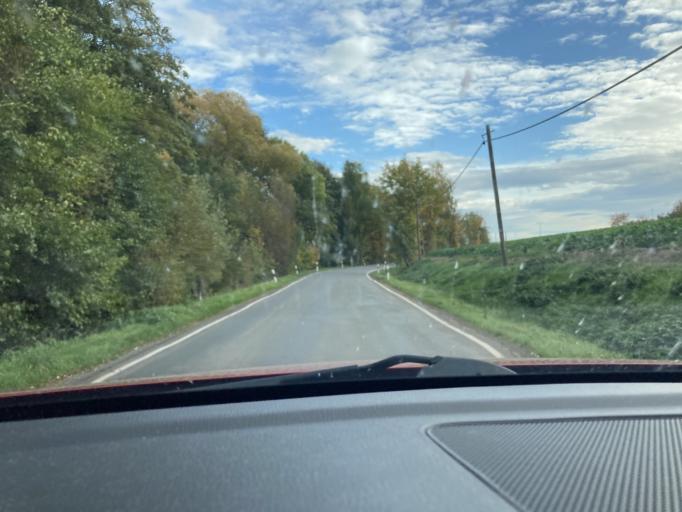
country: DE
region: Thuringia
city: Friedrichsthal
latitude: 51.5206
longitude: 10.5820
